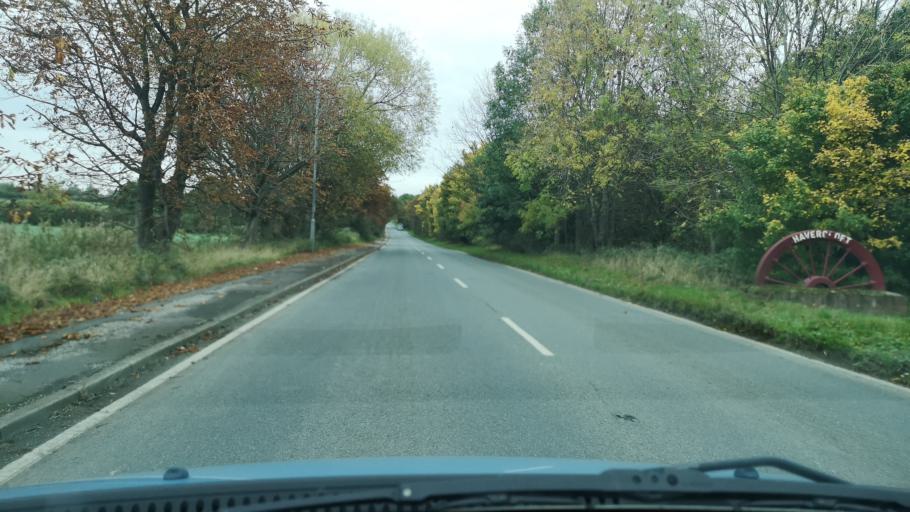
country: GB
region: England
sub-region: City and Borough of Wakefield
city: Ryhill
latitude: 53.6166
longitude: -1.4226
